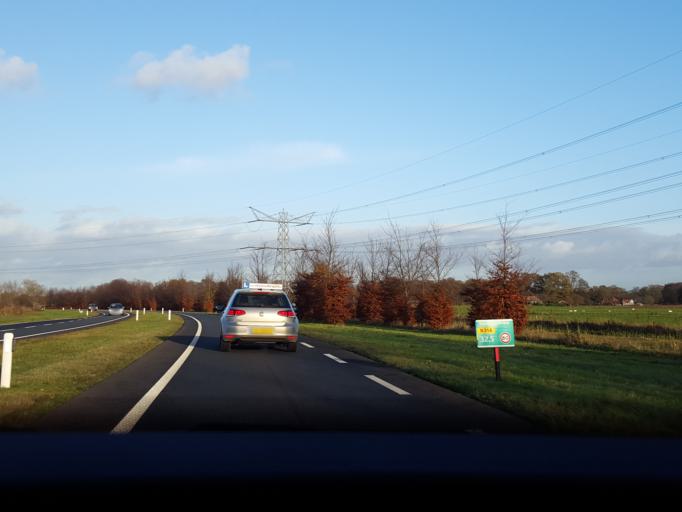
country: NL
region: Gelderland
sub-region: Gemeente Zutphen
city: Leesten
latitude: 52.1255
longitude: 6.2528
